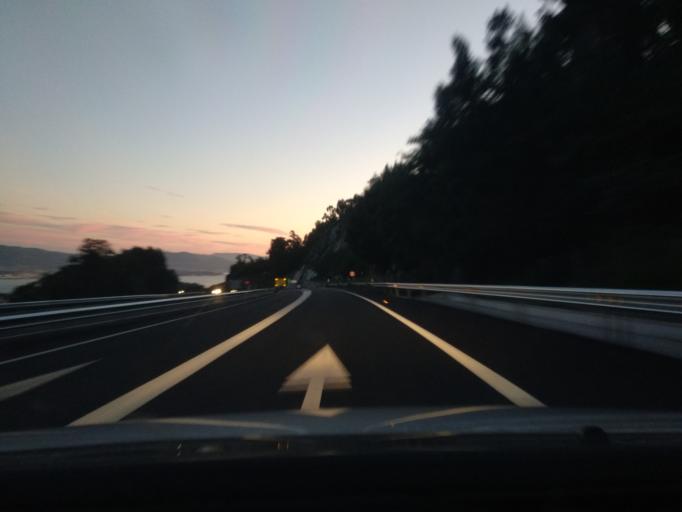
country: ES
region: Galicia
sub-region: Provincia de Pontevedra
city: Moana
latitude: 42.2928
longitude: -8.7529
